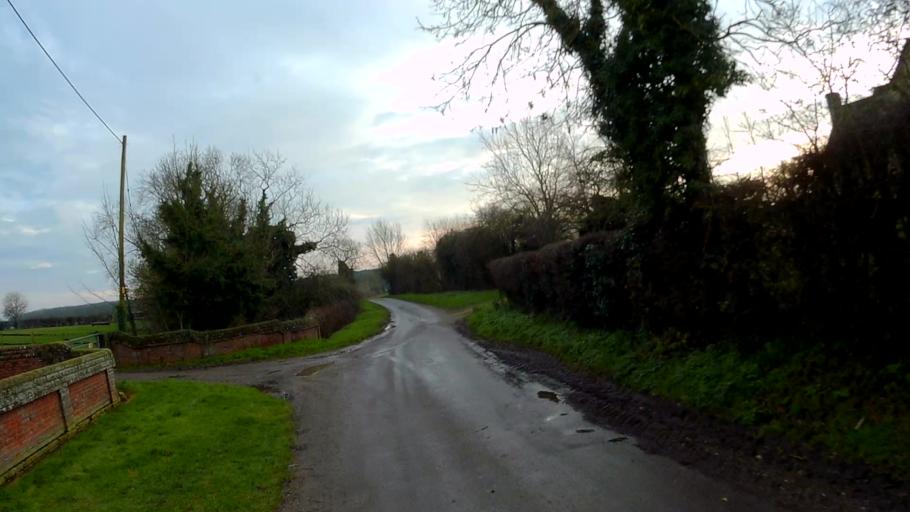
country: GB
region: England
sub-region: Lincolnshire
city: Bourne
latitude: 52.8302
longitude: -0.4059
